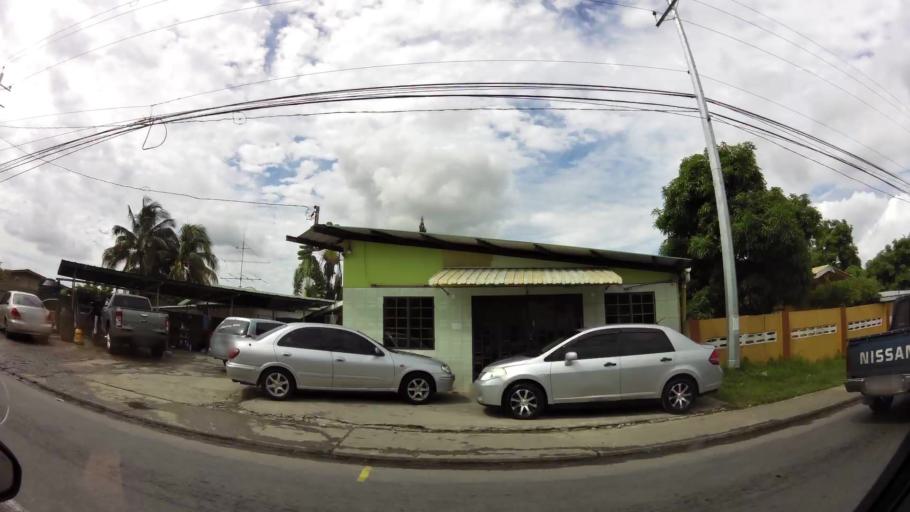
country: TT
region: Couva-Tabaquite-Talparo
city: Couva
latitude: 10.4184
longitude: -61.4708
